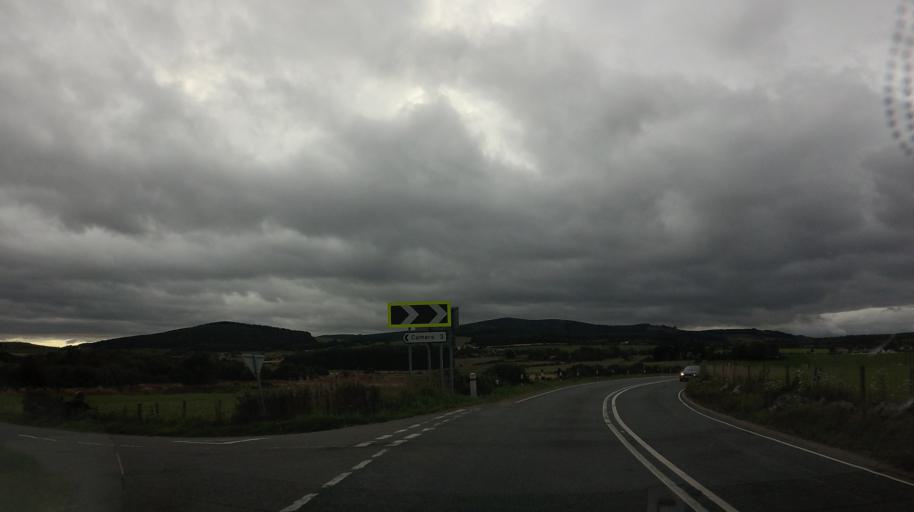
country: GB
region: Scotland
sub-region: Aberdeenshire
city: Kemnay
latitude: 57.1802
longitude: -2.5339
